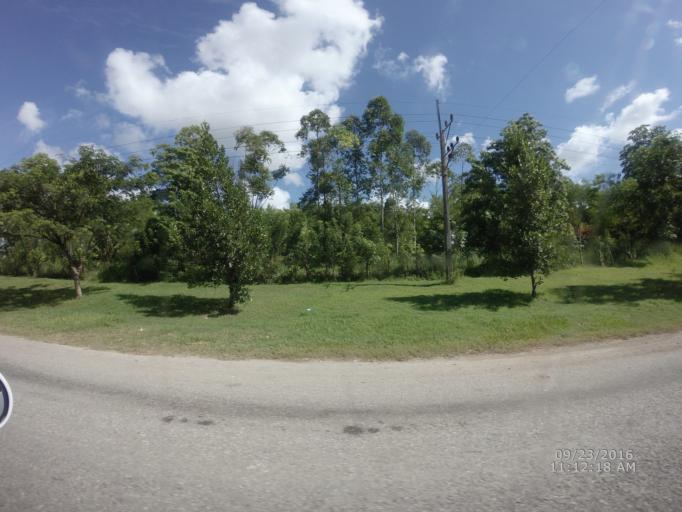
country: CU
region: La Habana
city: Arroyo Naranjo
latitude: 23.0289
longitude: -82.2818
